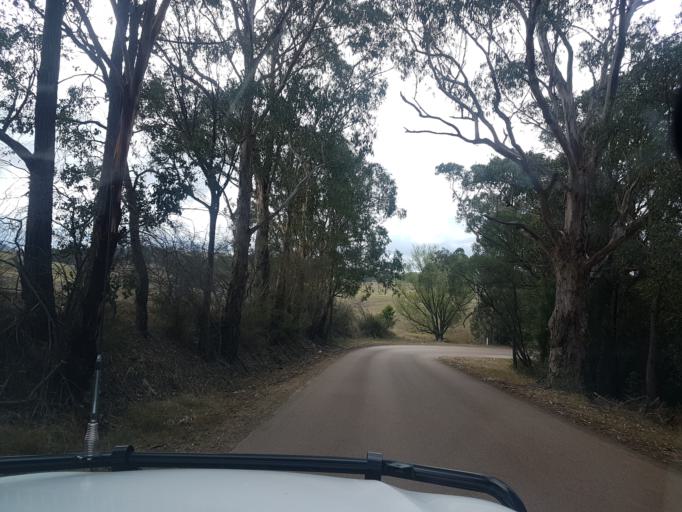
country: AU
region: Victoria
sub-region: East Gippsland
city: Bairnsdale
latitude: -37.7859
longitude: 147.5875
